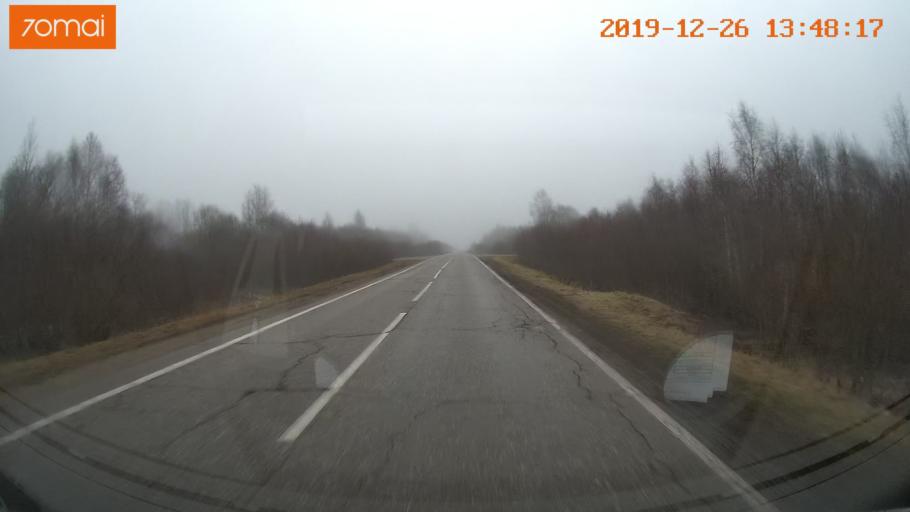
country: RU
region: Vologda
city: Sheksna
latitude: 58.6774
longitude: 38.5458
